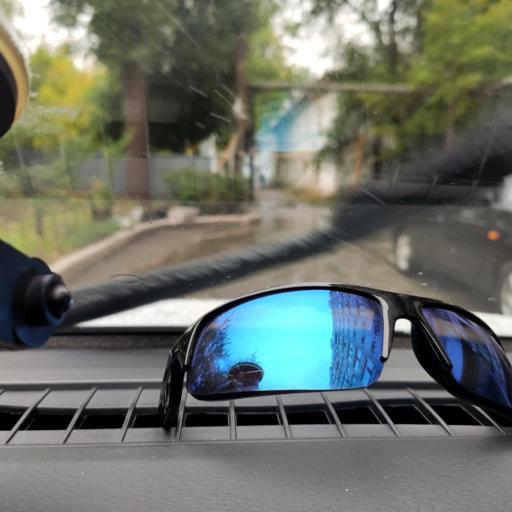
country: RU
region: Samara
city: Samara
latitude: 53.1188
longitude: 50.0753
